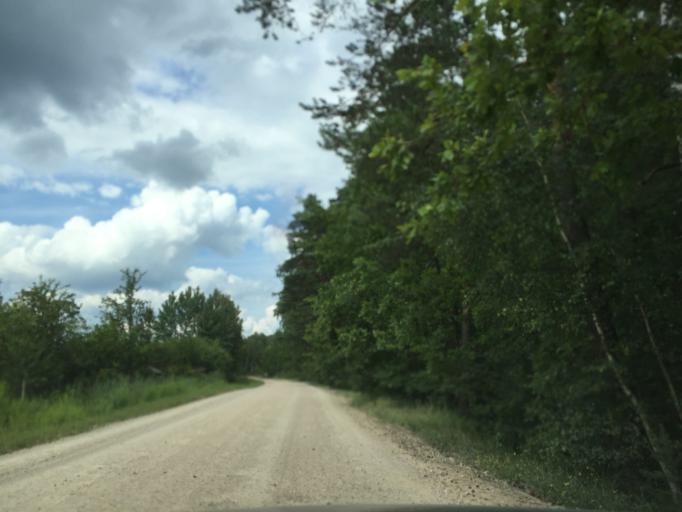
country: LV
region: Jelgava
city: Jelgava
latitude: 56.6327
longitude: 23.6235
